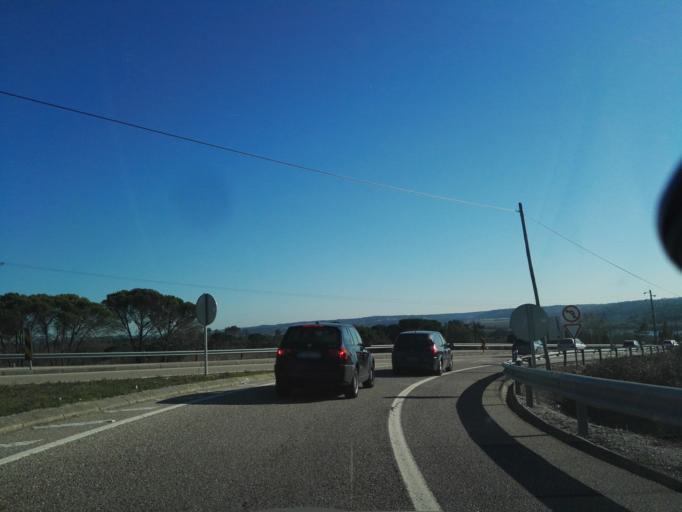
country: PT
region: Santarem
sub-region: Constancia
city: Constancia
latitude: 39.4842
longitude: -8.3264
